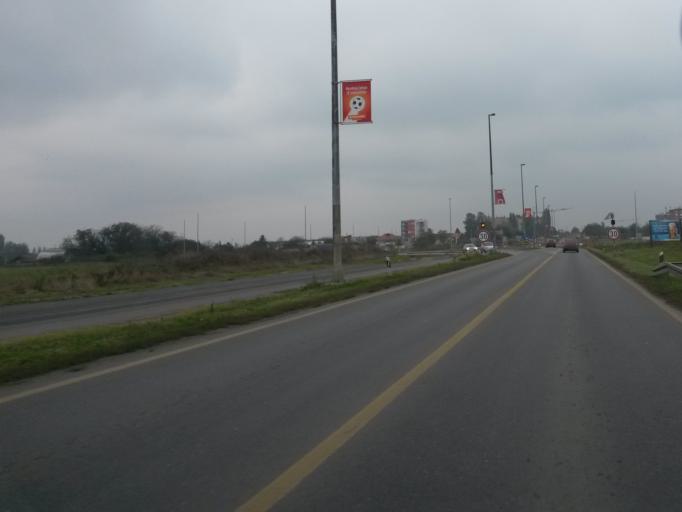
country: HR
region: Osjecko-Baranjska
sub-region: Grad Osijek
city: Osijek
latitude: 45.5421
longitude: 18.6814
